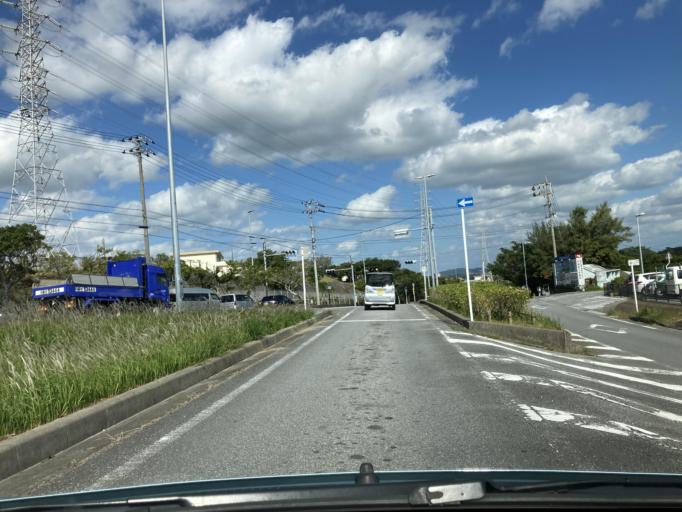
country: JP
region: Okinawa
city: Okinawa
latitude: 26.3420
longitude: 127.7988
